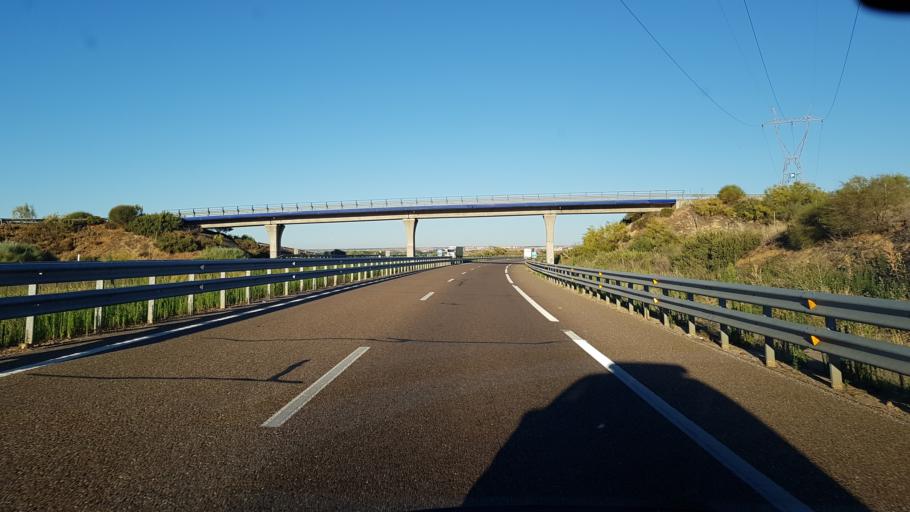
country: ES
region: Castille and Leon
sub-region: Provincia de Zamora
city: Coreses
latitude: 41.5418
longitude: -5.6595
